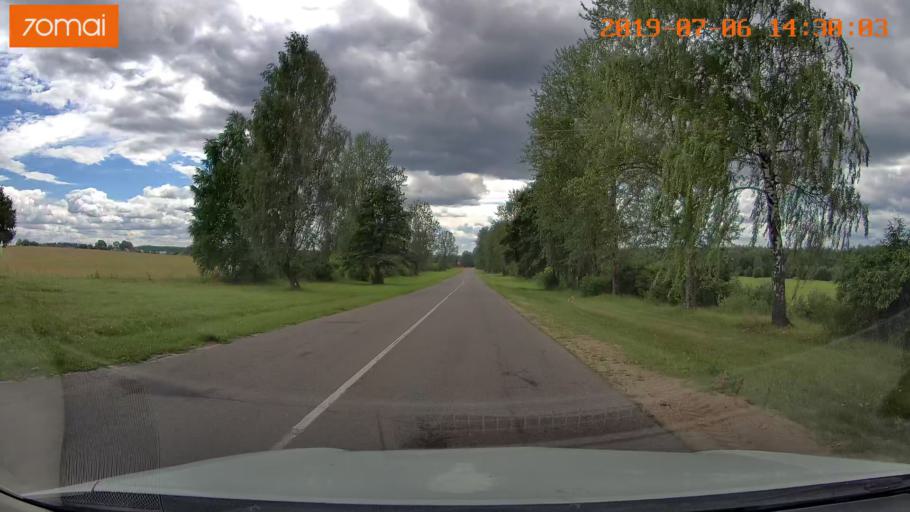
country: BY
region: Minsk
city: Ivyanyets
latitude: 53.9274
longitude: 26.7898
